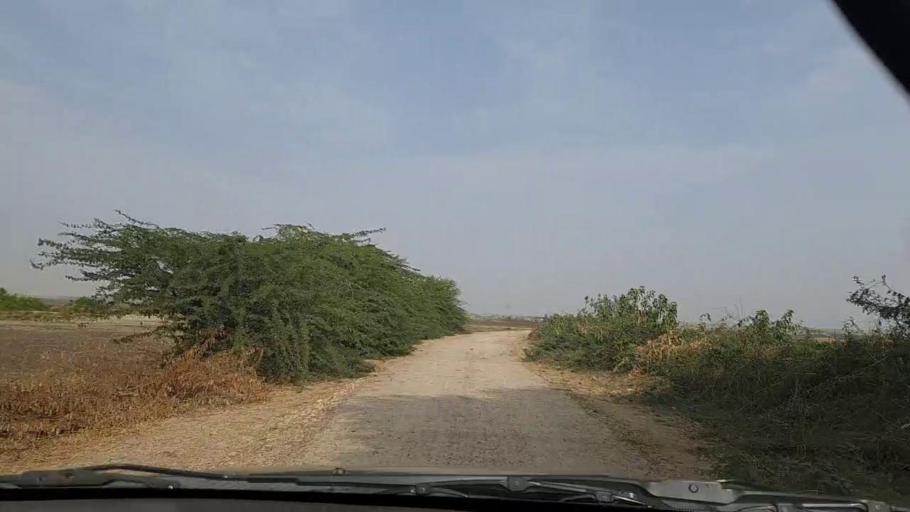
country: PK
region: Sindh
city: Thatta
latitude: 24.5740
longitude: 67.8517
